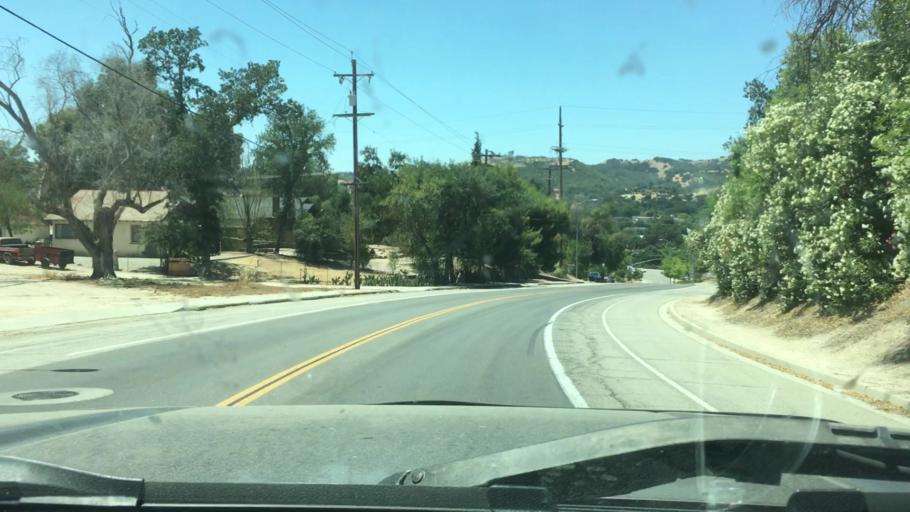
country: US
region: California
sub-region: San Luis Obispo County
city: Paso Robles
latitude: 35.6289
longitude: -120.6790
